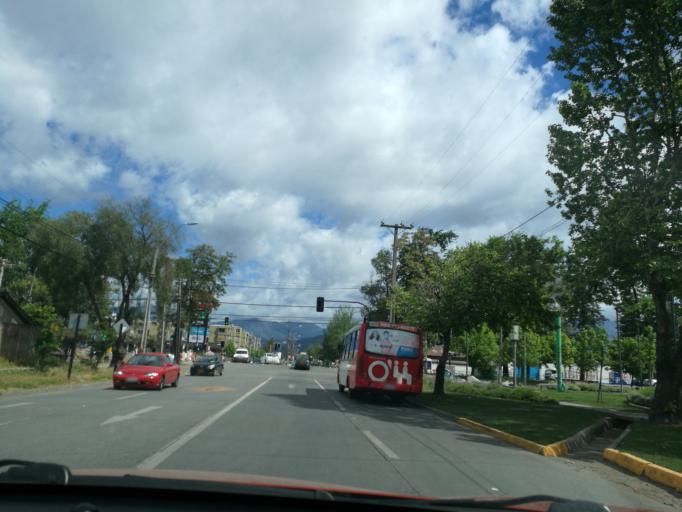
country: CL
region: O'Higgins
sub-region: Provincia de Cachapoal
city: Rancagua
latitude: -34.1397
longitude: -70.7347
